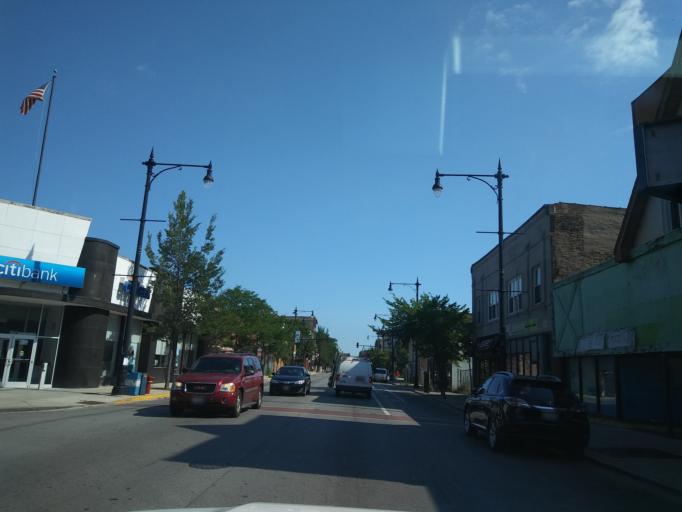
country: US
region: Illinois
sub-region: Cook County
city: Chicago
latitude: 41.8317
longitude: -87.6463
